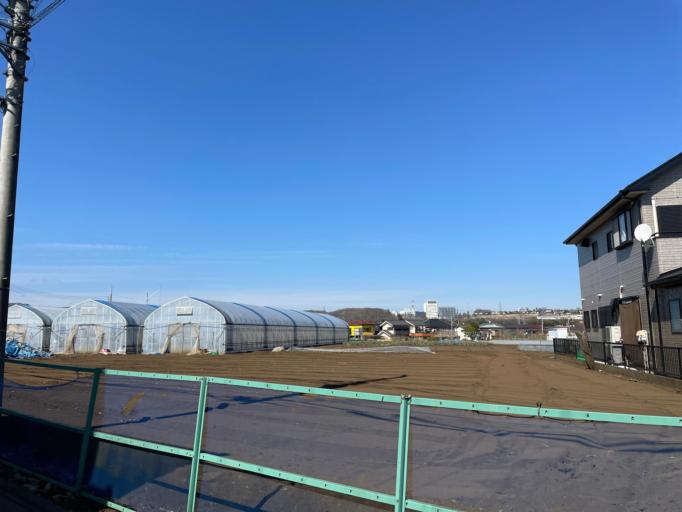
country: JP
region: Tokyo
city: Hachioji
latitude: 35.6737
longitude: 139.3177
